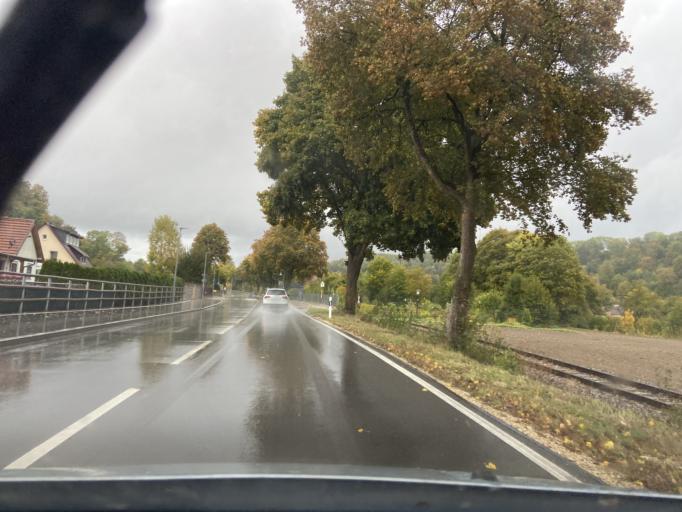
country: DE
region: Baden-Wuerttemberg
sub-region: Tuebingen Region
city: Sigmaringendorf
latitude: 48.0774
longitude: 9.2719
